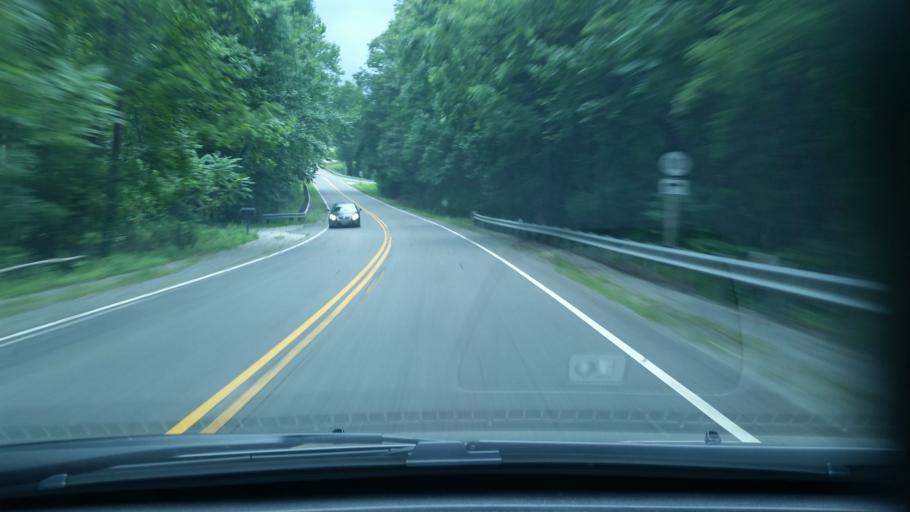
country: US
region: Virginia
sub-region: Nelson County
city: Nellysford
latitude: 37.8749
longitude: -78.8201
